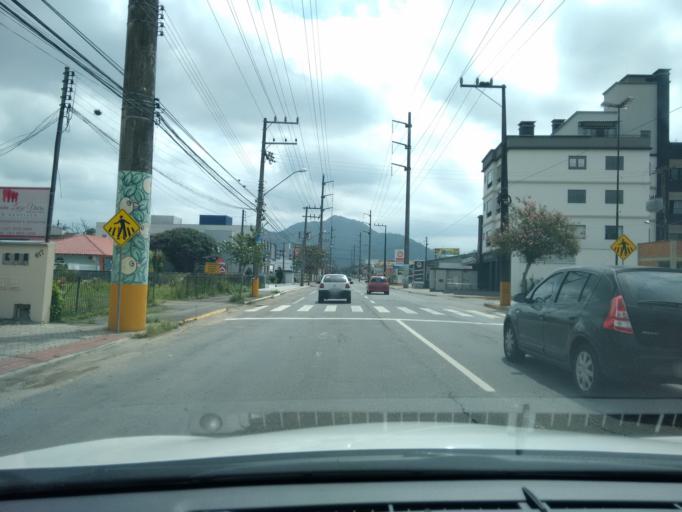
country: BR
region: Santa Catarina
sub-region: Jaragua Do Sul
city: Jaragua do Sul
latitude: -26.5113
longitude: -49.1156
